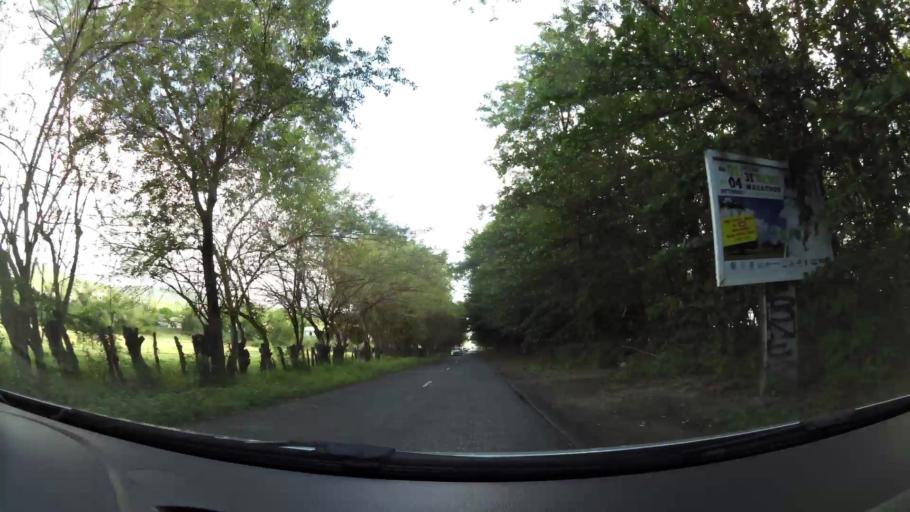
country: MQ
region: Martinique
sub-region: Martinique
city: Les Trois-Ilets
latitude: 14.4775
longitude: -61.0342
